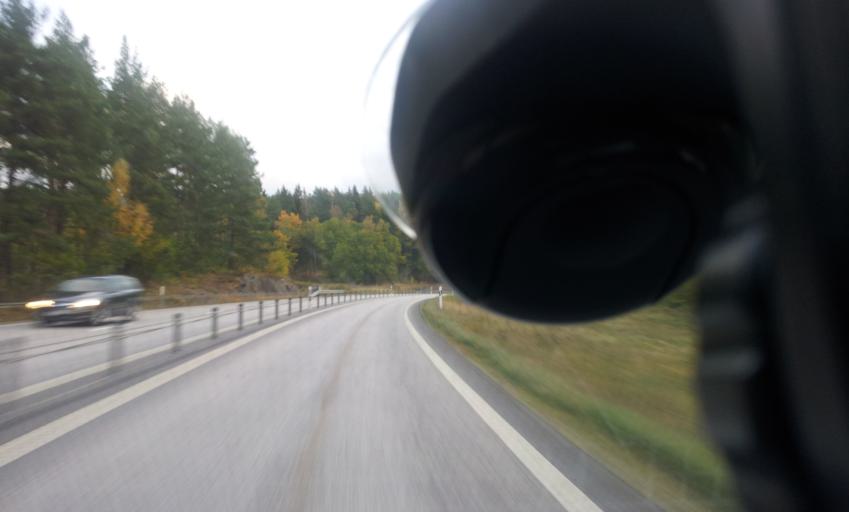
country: SE
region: Kalmar
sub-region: Vasterviks Kommun
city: Gamleby
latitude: 57.9287
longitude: 16.3978
